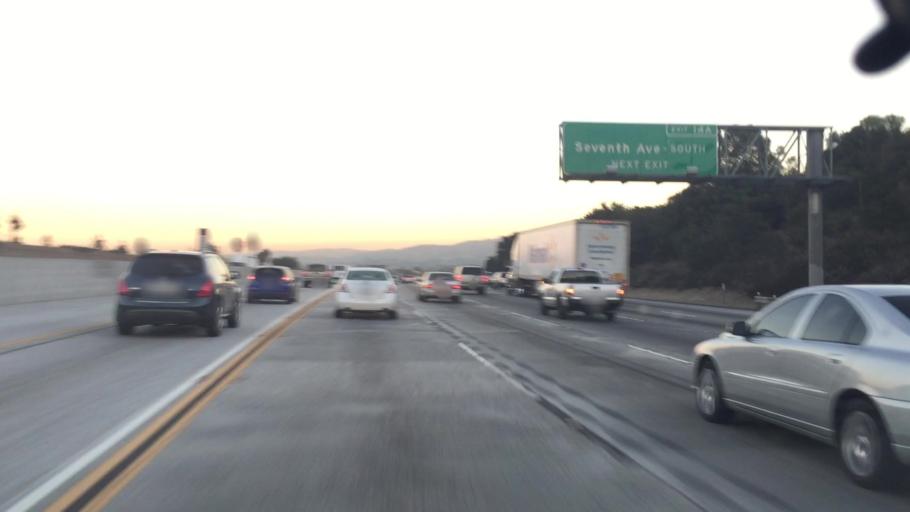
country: US
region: California
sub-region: Los Angeles County
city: Avocado Heights
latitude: 34.0251
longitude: -117.9941
